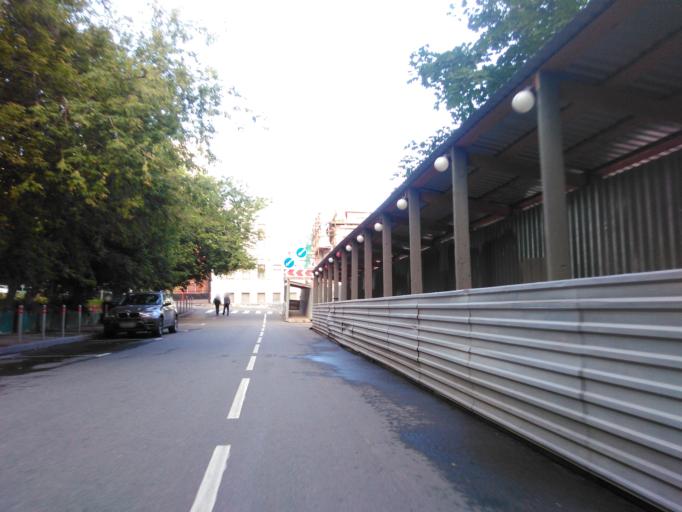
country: RU
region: Moscow
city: Zamoskvorech'ye
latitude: 55.7522
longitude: 37.6470
